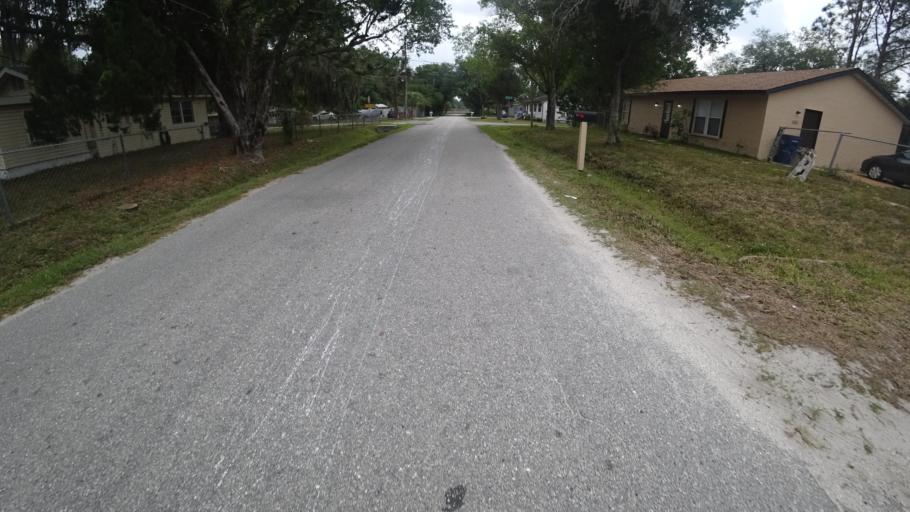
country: US
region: Florida
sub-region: Manatee County
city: Samoset
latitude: 27.4713
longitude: -82.5419
